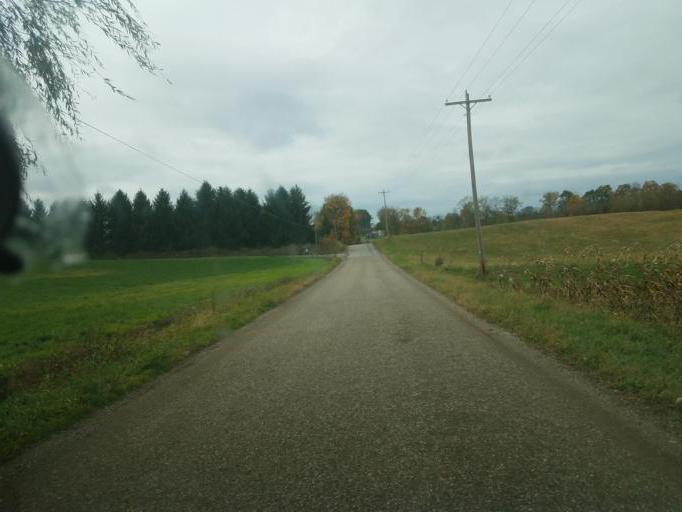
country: US
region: Ohio
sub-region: Wayne County
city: Shreve
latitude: 40.6243
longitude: -82.0968
